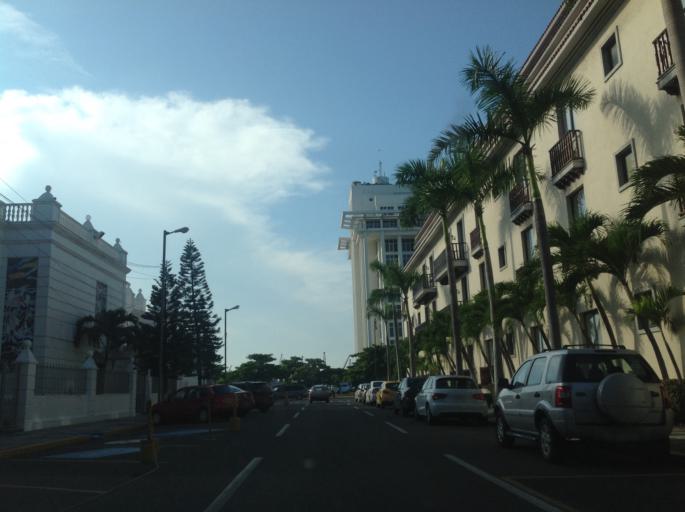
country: MX
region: Veracruz
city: Veracruz
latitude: 19.2010
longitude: -96.1319
